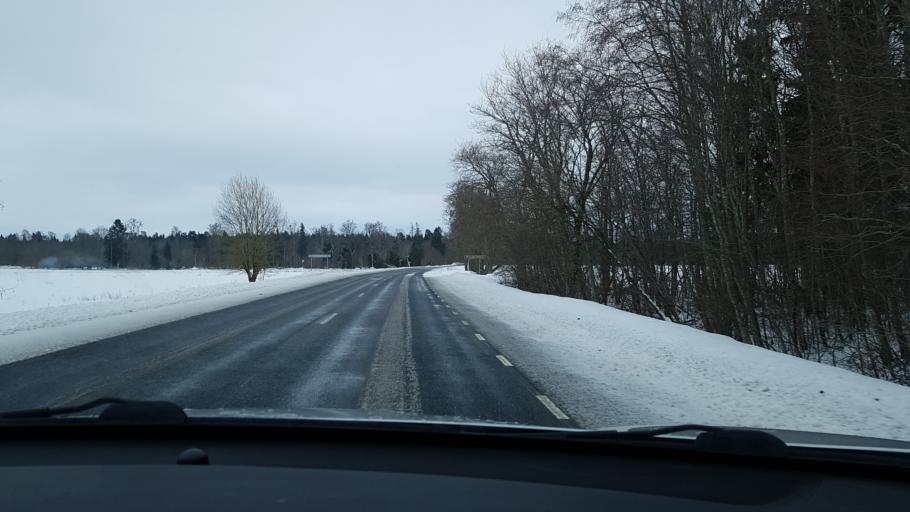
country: EE
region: Jaervamaa
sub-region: Jaerva-Jaani vald
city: Jarva-Jaani
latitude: 59.1021
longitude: 25.8144
